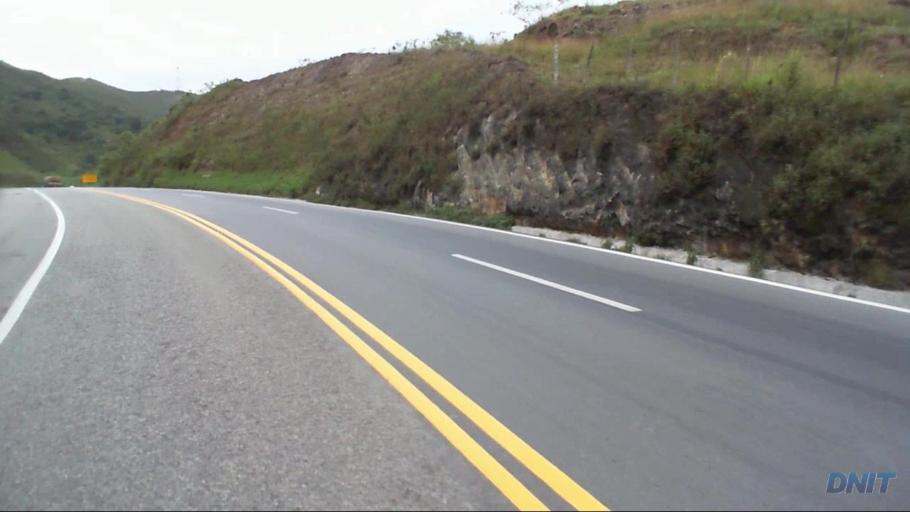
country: BR
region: Minas Gerais
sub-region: Nova Era
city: Nova Era
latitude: -19.6886
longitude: -42.9903
